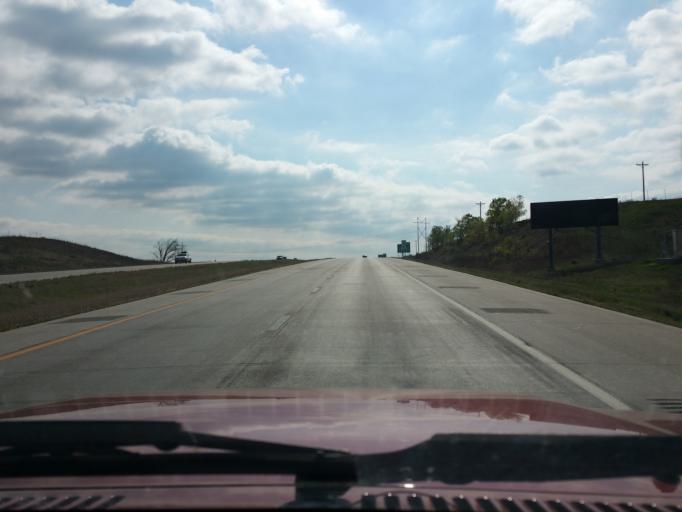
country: US
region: Kansas
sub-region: Riley County
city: Manhattan
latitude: 39.0653
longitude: -96.5086
